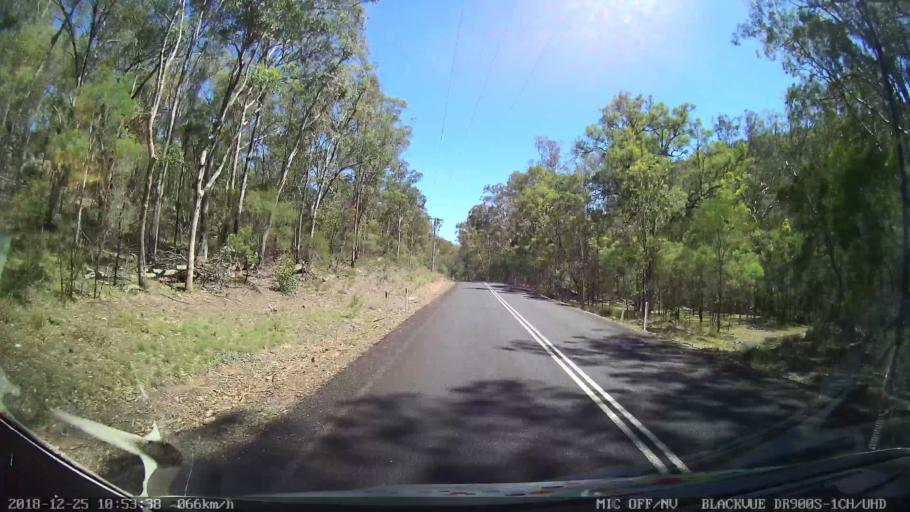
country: AU
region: New South Wales
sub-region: Upper Hunter Shire
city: Merriwa
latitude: -32.4180
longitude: 150.2732
